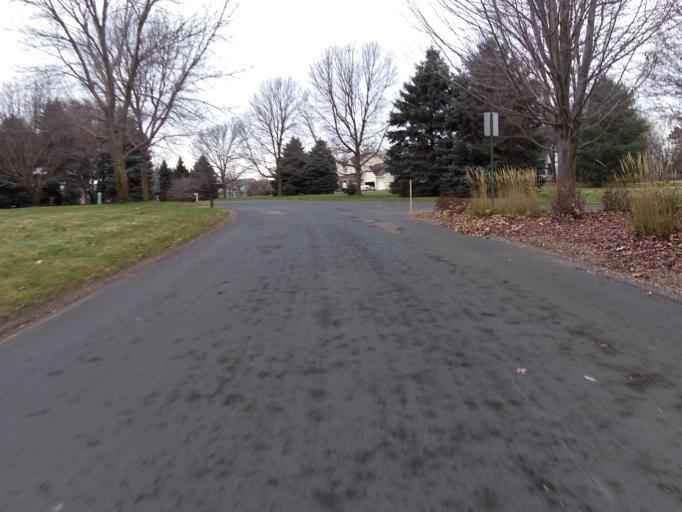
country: US
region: Minnesota
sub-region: Washington County
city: Lake Elmo
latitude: 44.9893
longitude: -92.8703
